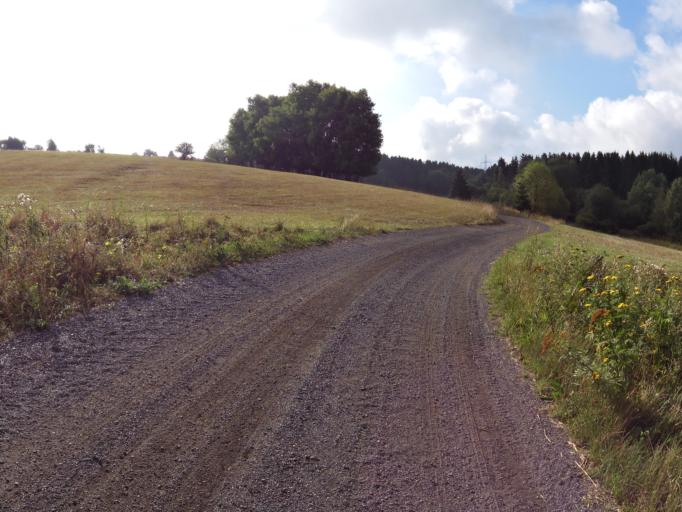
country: DE
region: North Rhine-Westphalia
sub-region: Regierungsbezirk Koln
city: Blankenheim
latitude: 50.4436
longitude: 6.6051
